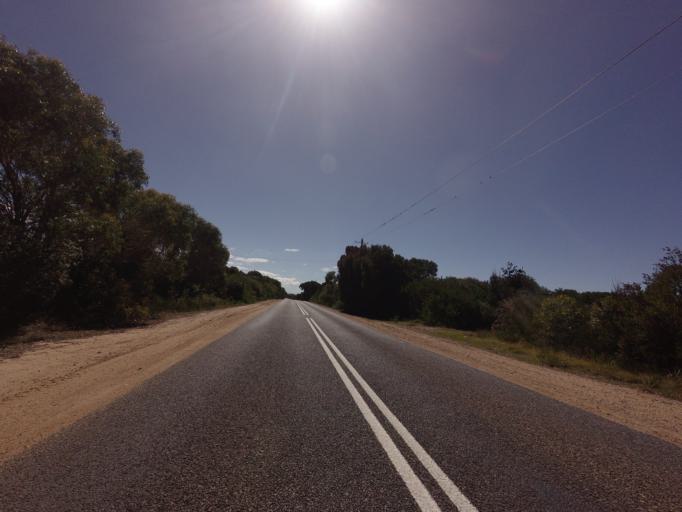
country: AU
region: Tasmania
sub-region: Break O'Day
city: St Helens
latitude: -41.8256
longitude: 148.2629
